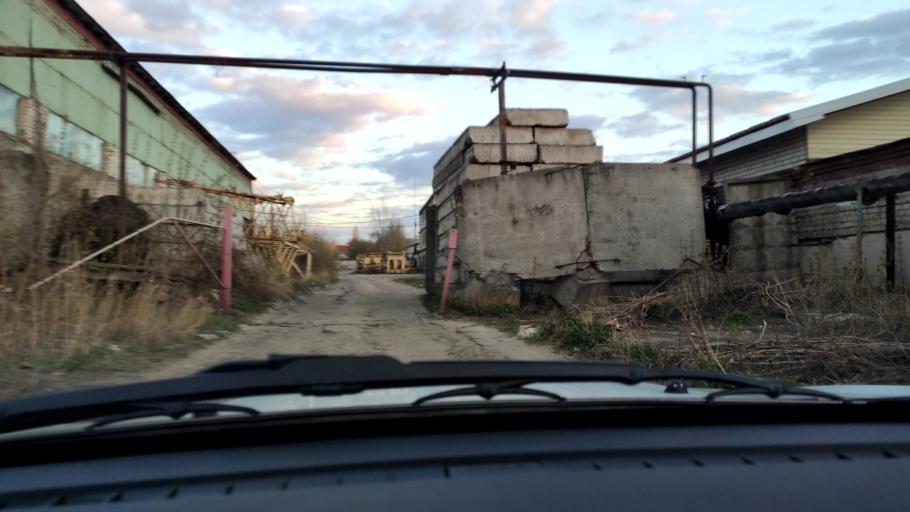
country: RU
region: Voronezj
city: Voronezh
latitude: 51.6865
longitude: 39.1454
